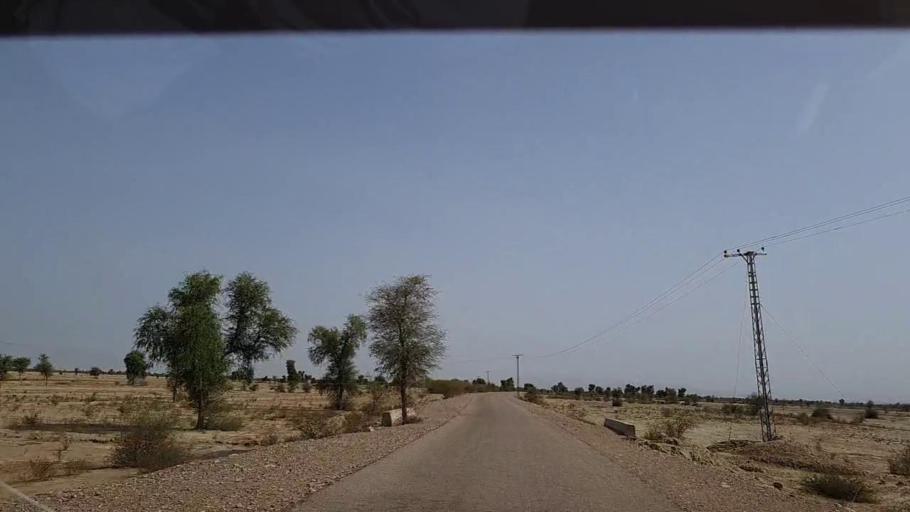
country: PK
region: Sindh
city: Johi
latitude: 26.6592
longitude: 67.5060
